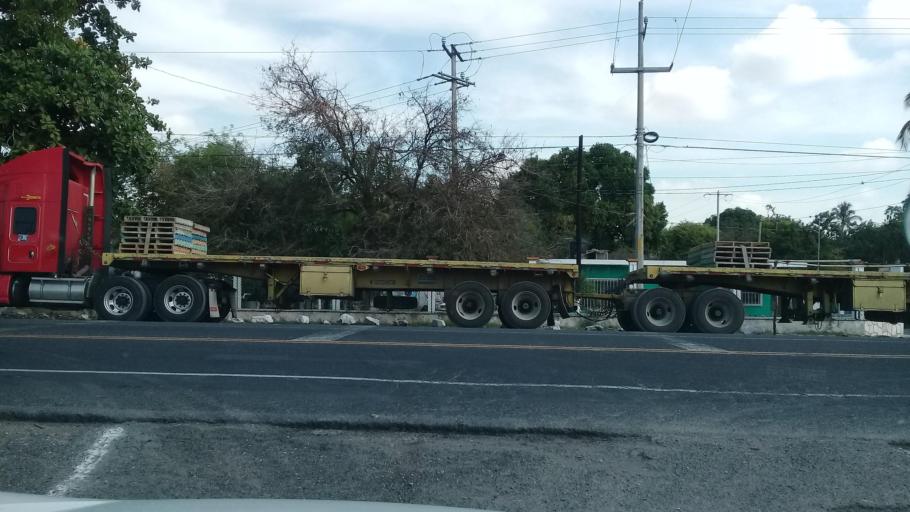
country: MX
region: Veracruz
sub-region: Emiliano Zapata
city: Plan del Rio
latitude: 19.3898
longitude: -96.6383
